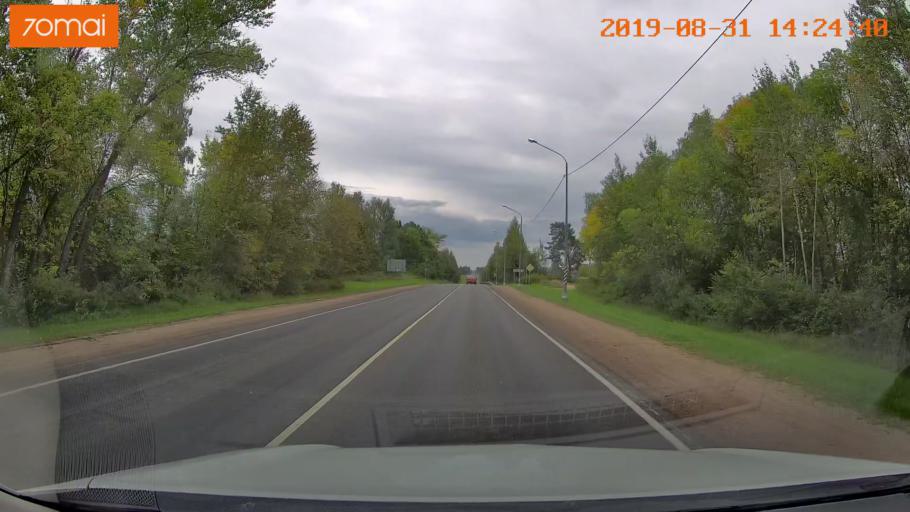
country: RU
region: Smolensk
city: Yekimovichi
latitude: 54.1042
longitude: 33.2597
